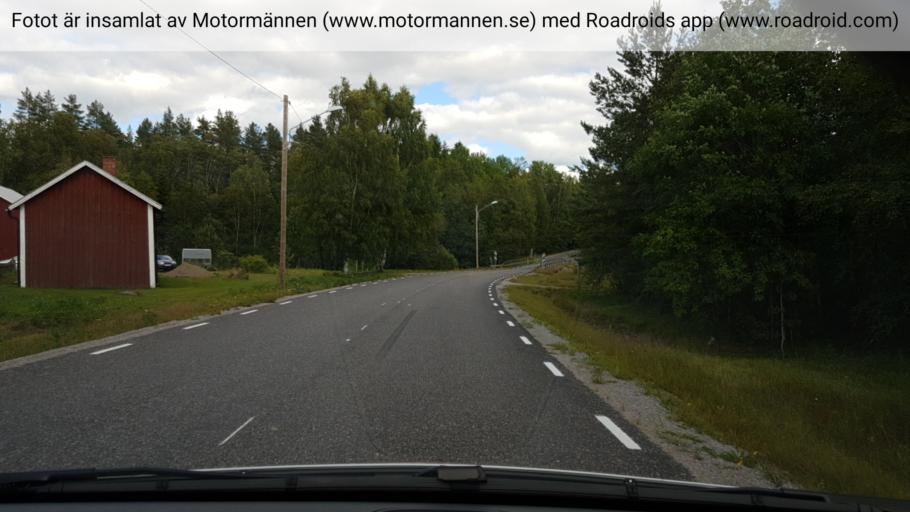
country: SE
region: Vaesterbotten
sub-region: Umea Kommun
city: Hoernefors
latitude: 63.6854
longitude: 19.8928
